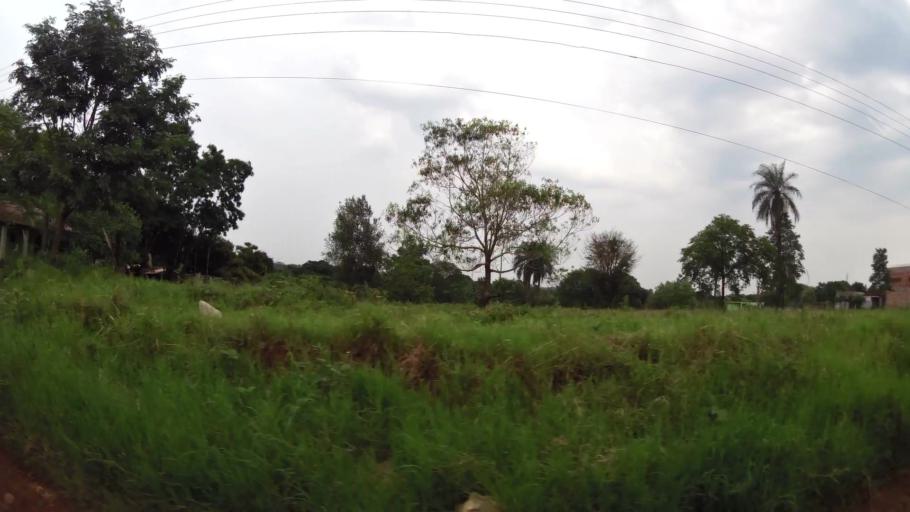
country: PY
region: Alto Parana
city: Presidente Franco
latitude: -25.5425
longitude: -54.6522
